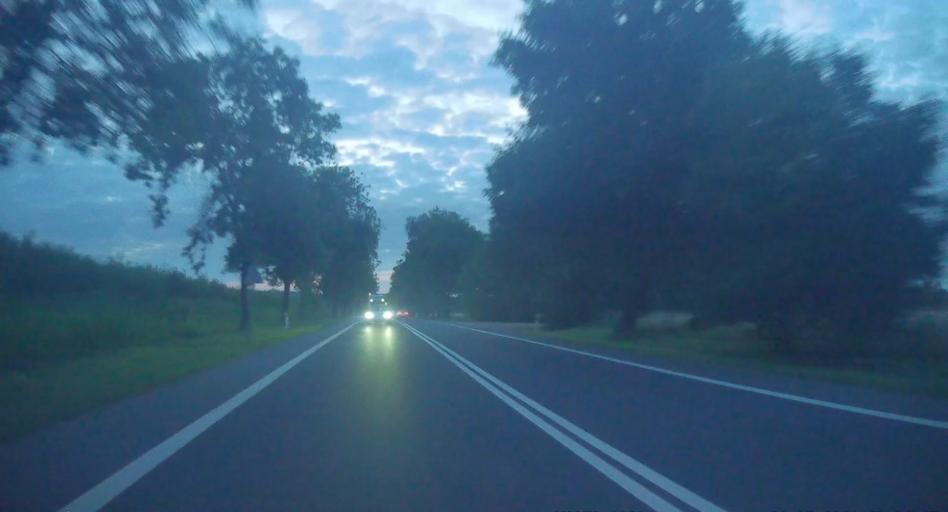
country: PL
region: Silesian Voivodeship
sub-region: Powiat klobucki
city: Klobuck
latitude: 50.9167
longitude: 18.8897
